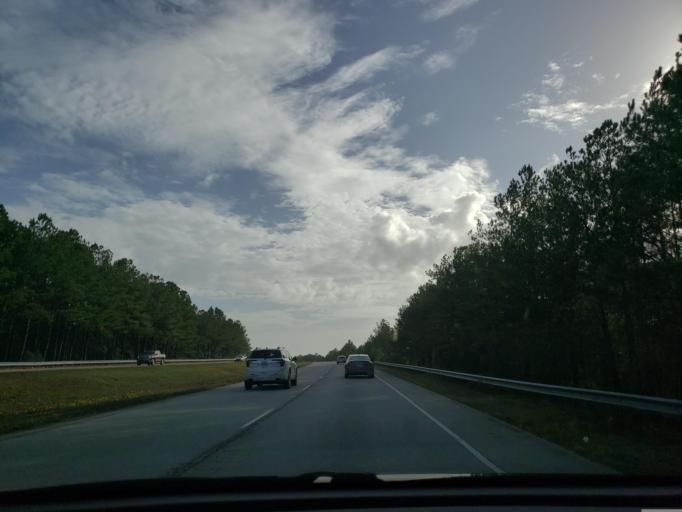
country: US
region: North Carolina
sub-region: Onslow County
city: Sneads Ferry
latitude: 34.6183
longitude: -77.4842
